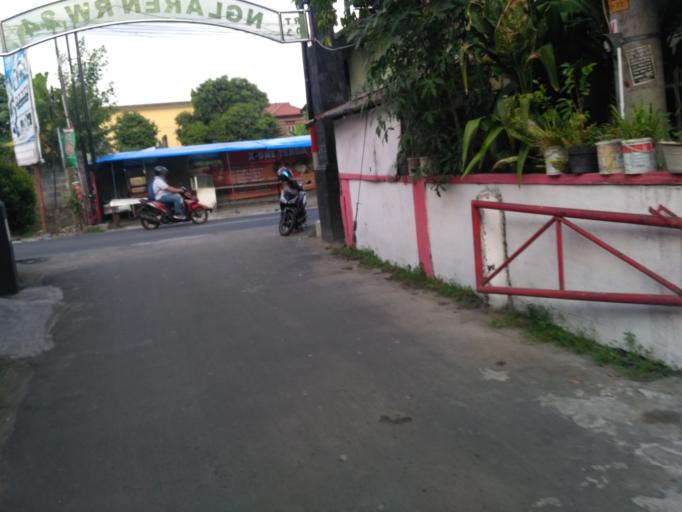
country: ID
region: Daerah Istimewa Yogyakarta
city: Depok
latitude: -7.7641
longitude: 110.4059
